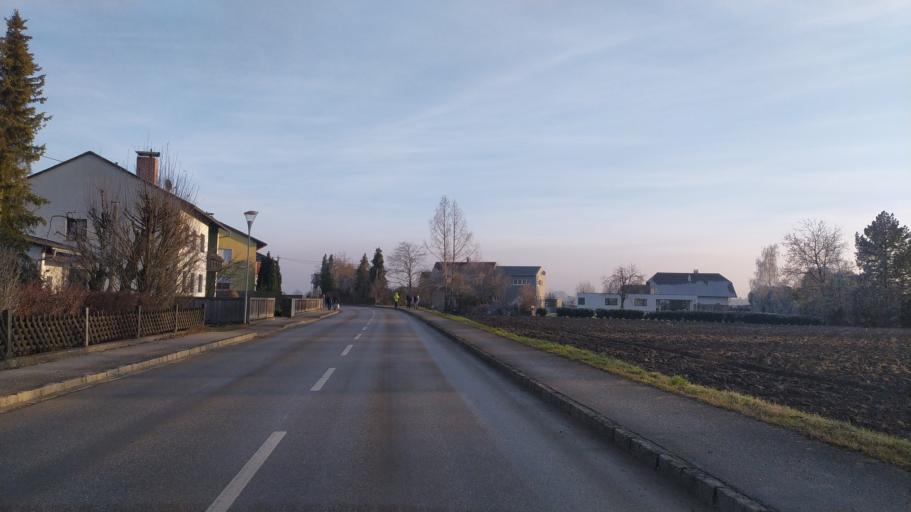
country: AT
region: Upper Austria
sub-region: Politischer Bezirk Urfahr-Umgebung
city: Feldkirchen an der Donau
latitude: 48.3475
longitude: 14.0719
